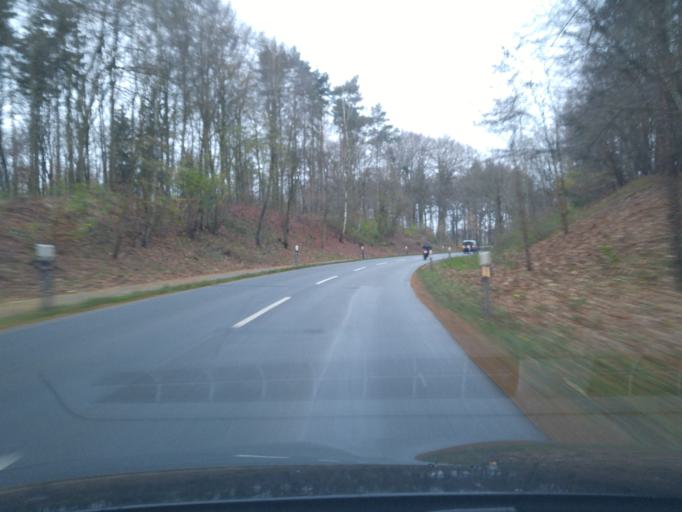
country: DE
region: Lower Saxony
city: Scharnebeck
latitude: 53.2769
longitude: 10.5032
